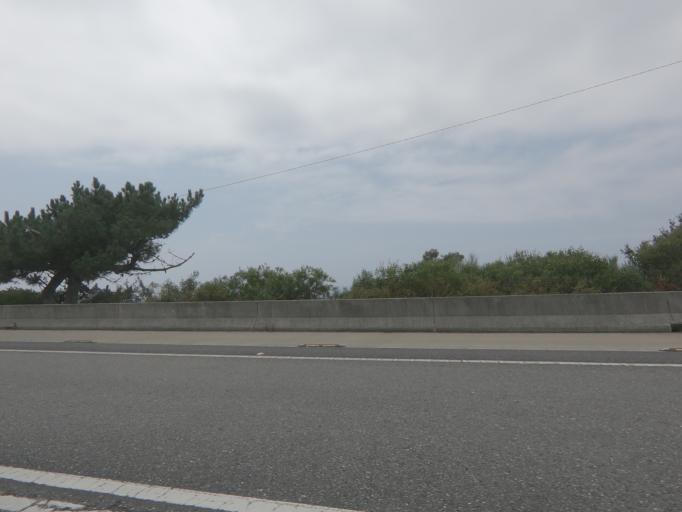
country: ES
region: Galicia
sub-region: Provincia de Pontevedra
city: Oia
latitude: 41.9851
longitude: -8.8842
